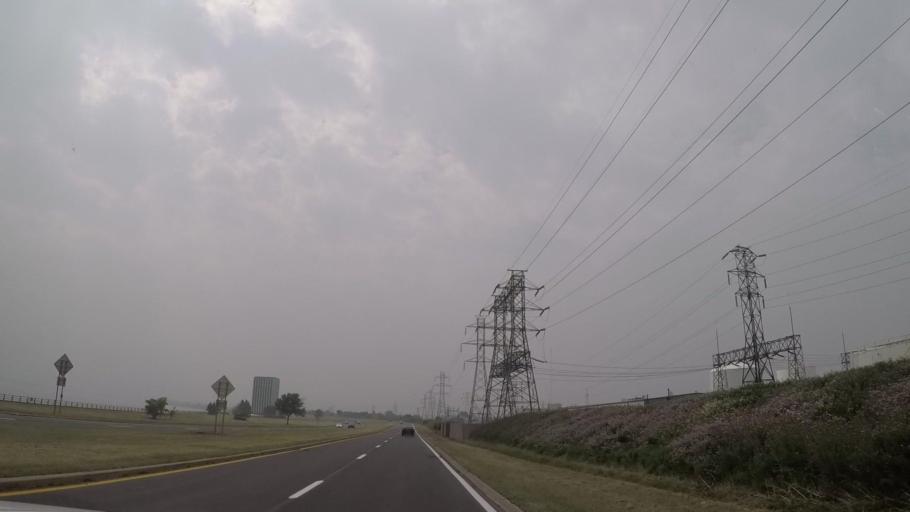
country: US
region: New York
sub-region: Niagara County
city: Niagara Falls
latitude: 43.0764
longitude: -79.0095
